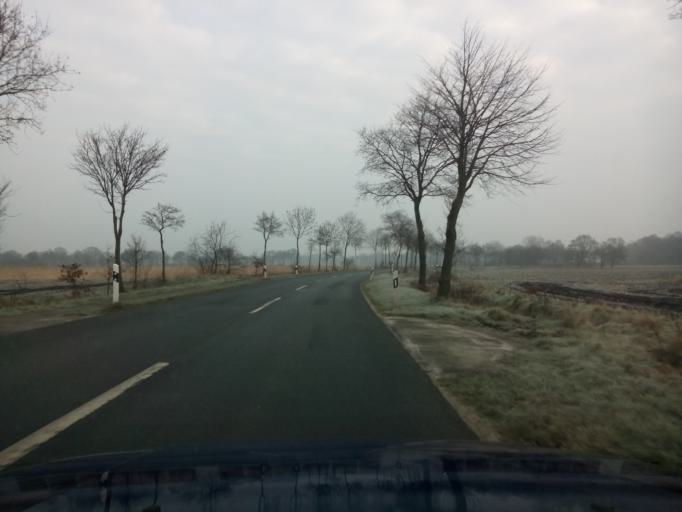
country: DE
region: Lower Saxony
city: Langen
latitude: 53.5848
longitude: 8.6399
